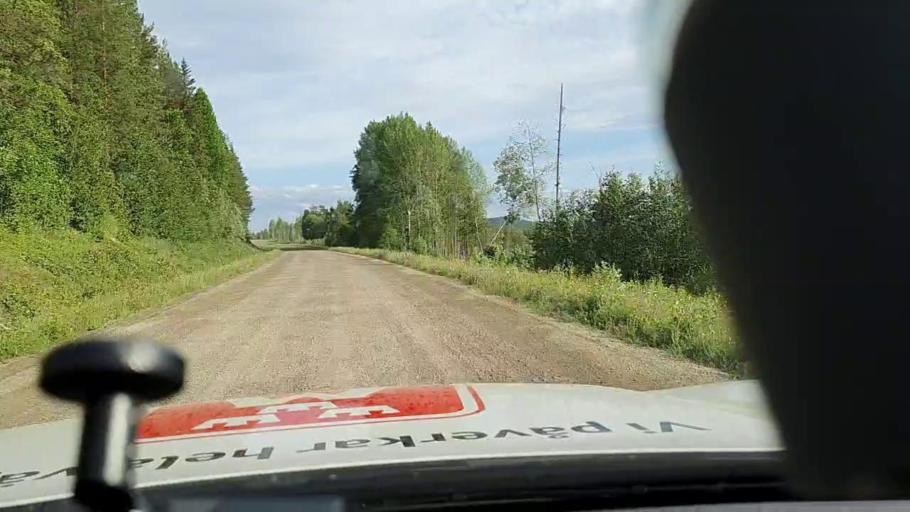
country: SE
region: Norrbotten
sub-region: Alvsbyns Kommun
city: AElvsbyn
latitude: 66.1897
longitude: 21.1986
